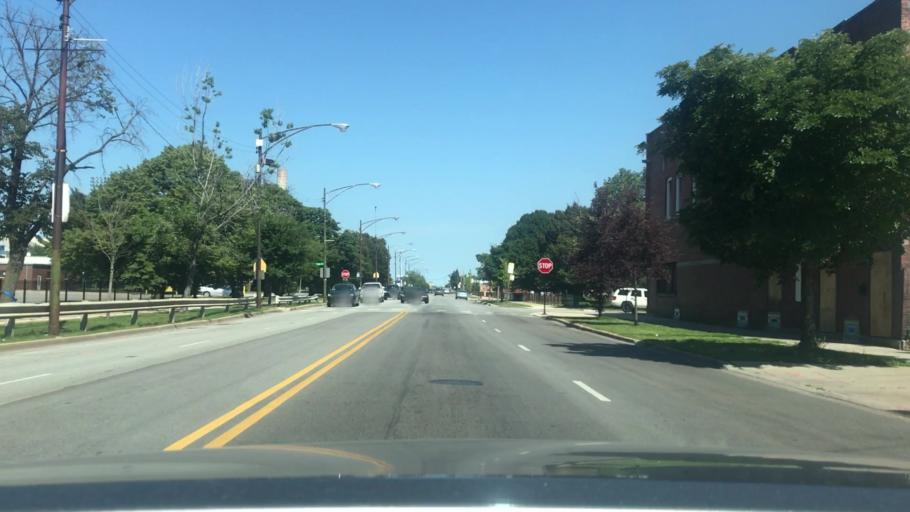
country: US
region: Illinois
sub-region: Cook County
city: Dolton
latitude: 41.7075
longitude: -87.6049
